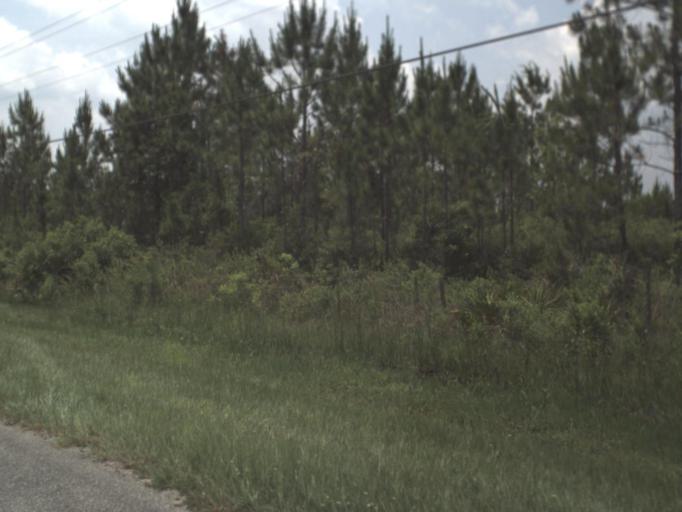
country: US
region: Florida
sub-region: Putnam County
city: Palatka
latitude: 29.5892
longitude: -81.7152
